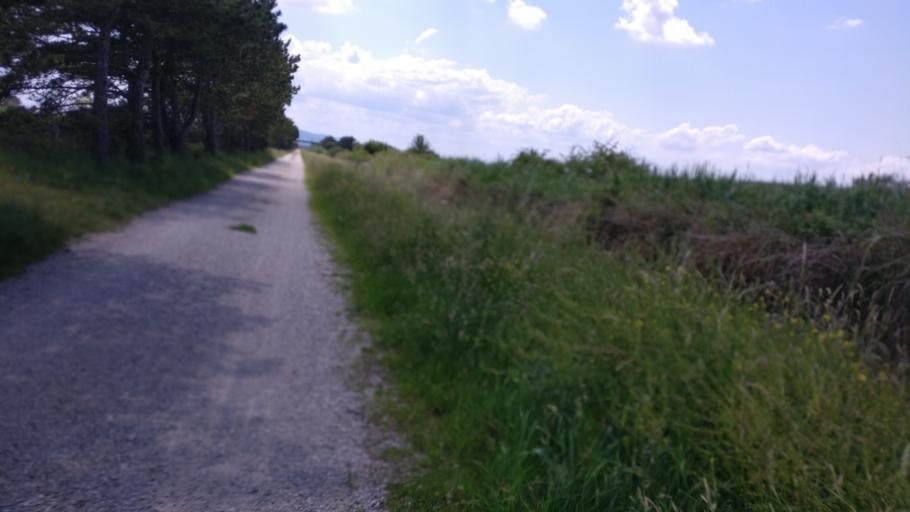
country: AT
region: Lower Austria
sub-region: Politischer Bezirk Wiener Neustadt
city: Sollenau
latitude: 47.8817
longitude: 16.2803
